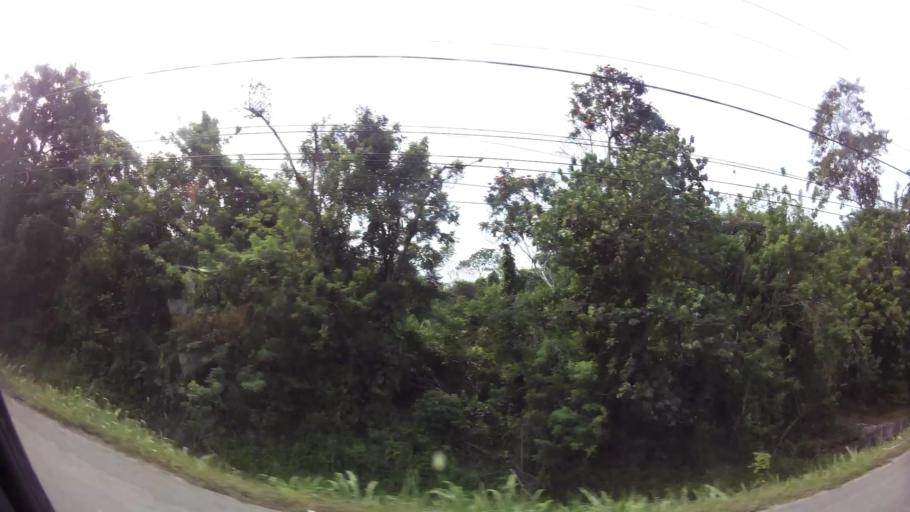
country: HN
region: Atlantida
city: Tela
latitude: 15.7697
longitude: -87.4529
